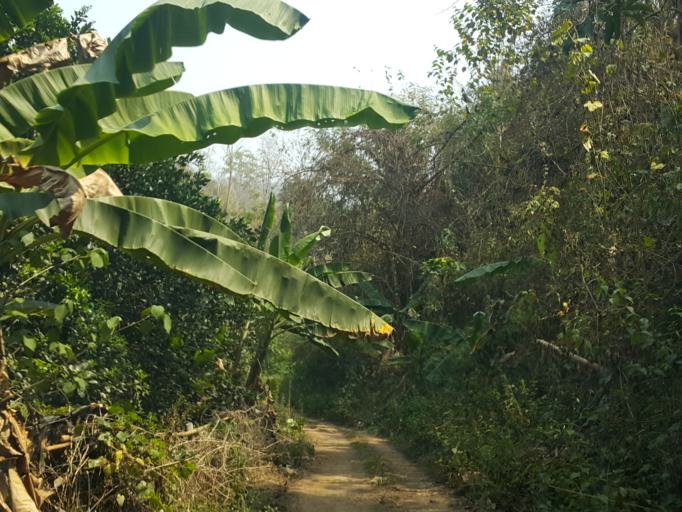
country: TH
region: Chiang Mai
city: Hang Dong
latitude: 18.7569
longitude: 98.8234
